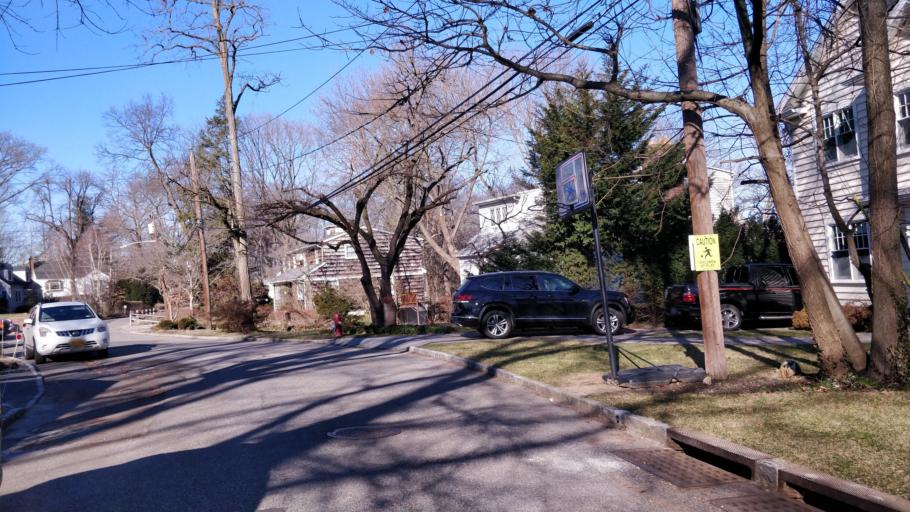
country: US
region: New York
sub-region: Nassau County
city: Glen Head
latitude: 40.8405
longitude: -73.6171
